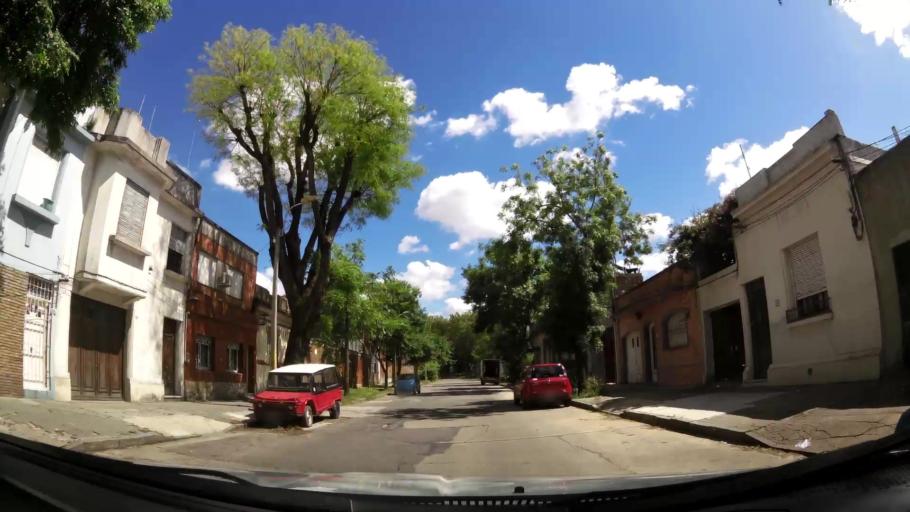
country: UY
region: Montevideo
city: Montevideo
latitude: -34.8787
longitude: -56.1928
